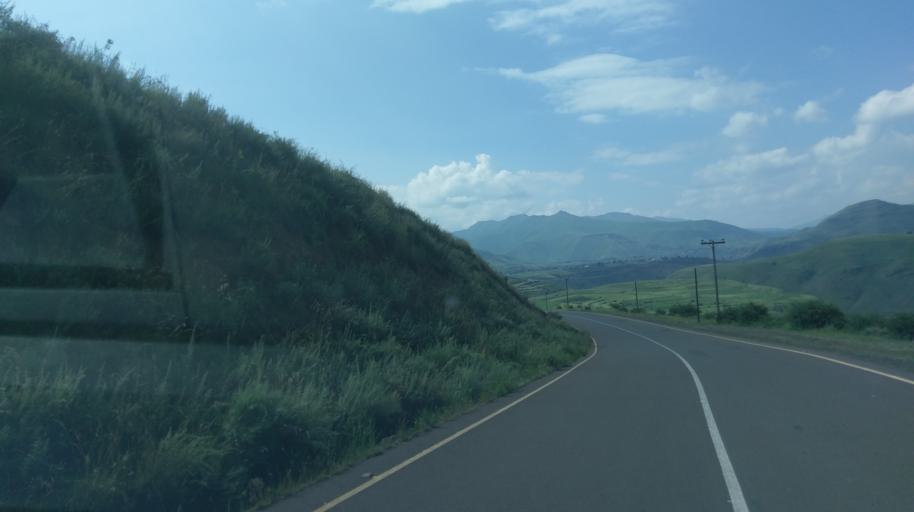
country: LS
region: Thaba-Tseka
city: Thaba-Tseka
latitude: -29.1360
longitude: 28.4938
